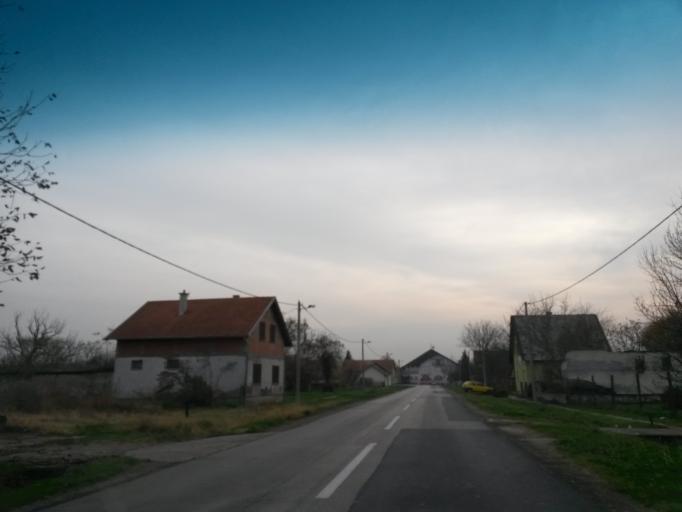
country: HR
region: Vukovarsko-Srijemska
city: Nijemci
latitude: 45.1840
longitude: 19.0134
